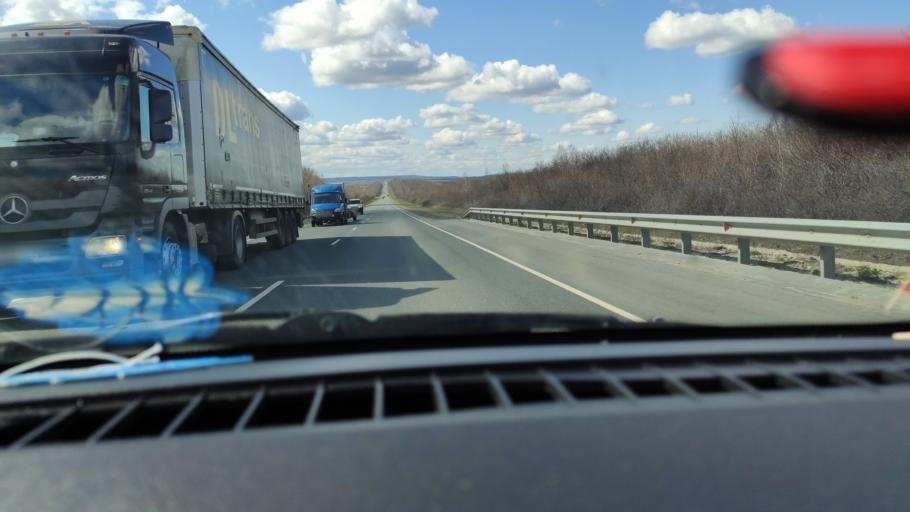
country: RU
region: Saratov
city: Khvalynsk
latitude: 52.6121
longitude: 48.1605
